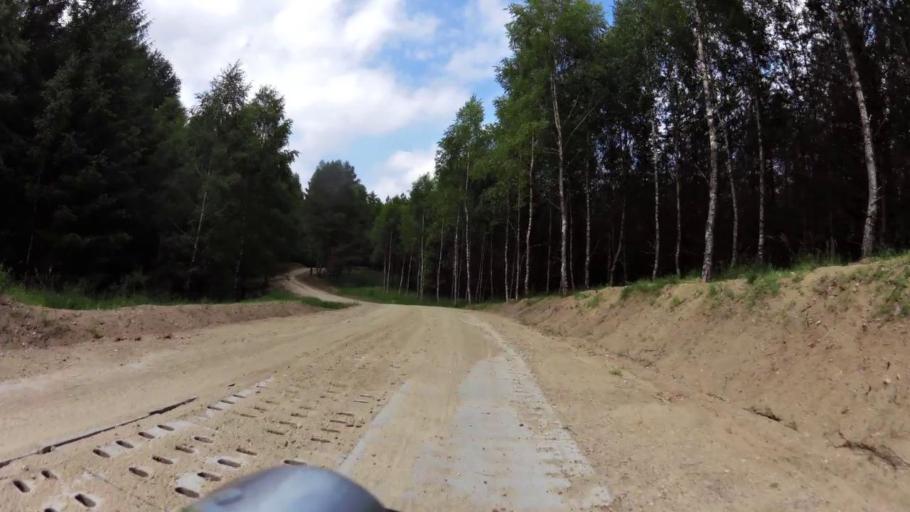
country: PL
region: West Pomeranian Voivodeship
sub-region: Powiat szczecinecki
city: Bialy Bor
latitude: 53.9561
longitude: 16.7573
